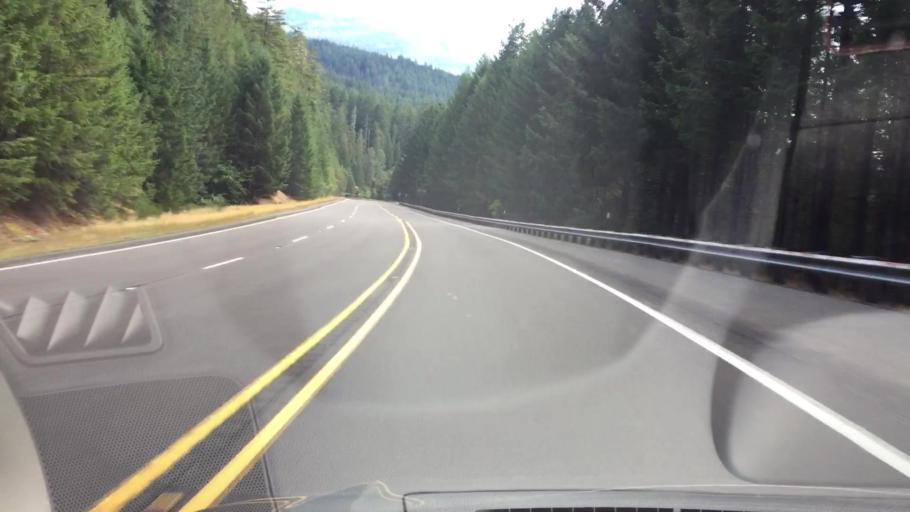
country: US
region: Washington
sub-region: Pierce County
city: Buckley
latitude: 46.6600
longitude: -121.6014
